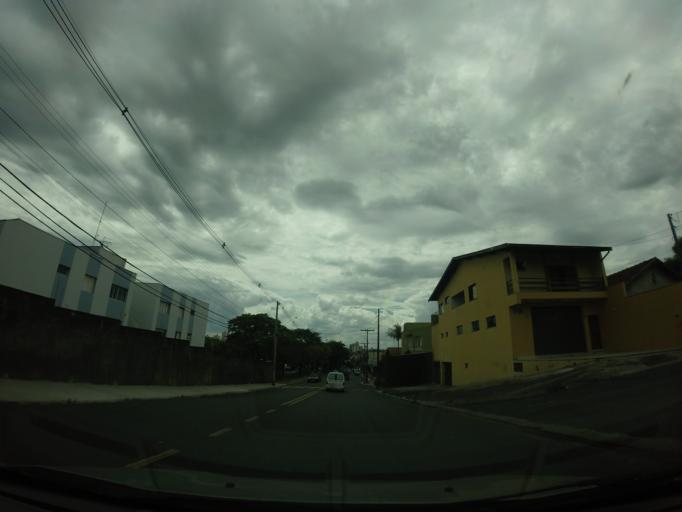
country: BR
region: Sao Paulo
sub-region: Piracicaba
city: Piracicaba
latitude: -22.7436
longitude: -47.6238
